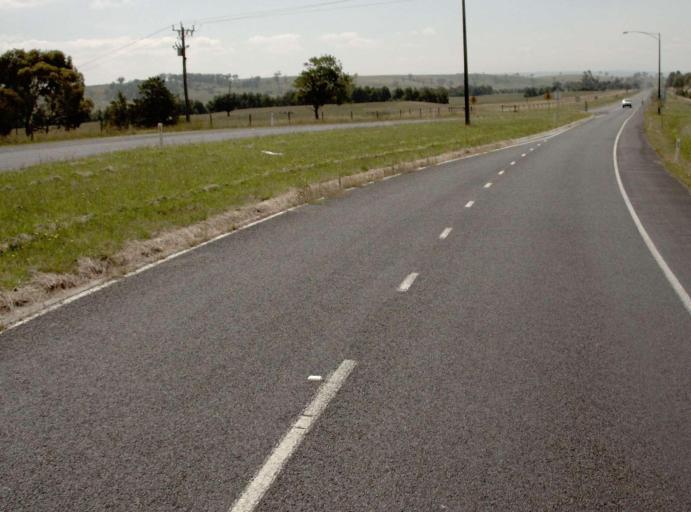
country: AU
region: Victoria
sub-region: Latrobe
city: Traralgon
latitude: -38.2483
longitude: 146.5481
